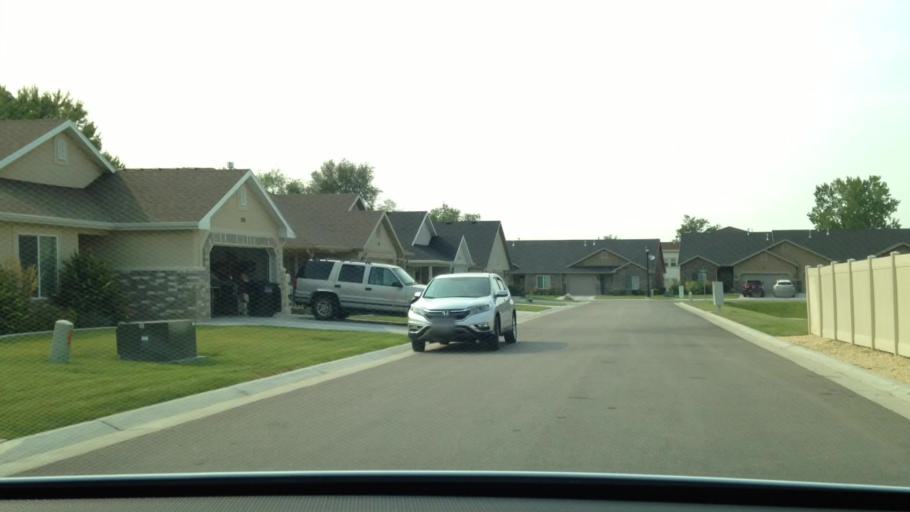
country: US
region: Utah
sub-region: Davis County
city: Kaysville
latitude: 41.0440
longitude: -111.9479
